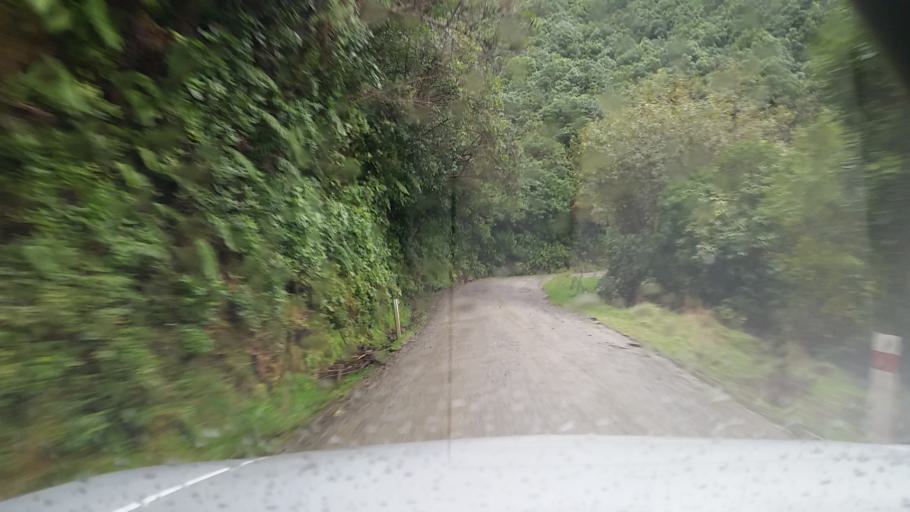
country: NZ
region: Marlborough
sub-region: Marlborough District
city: Picton
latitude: -41.1394
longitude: 174.0498
